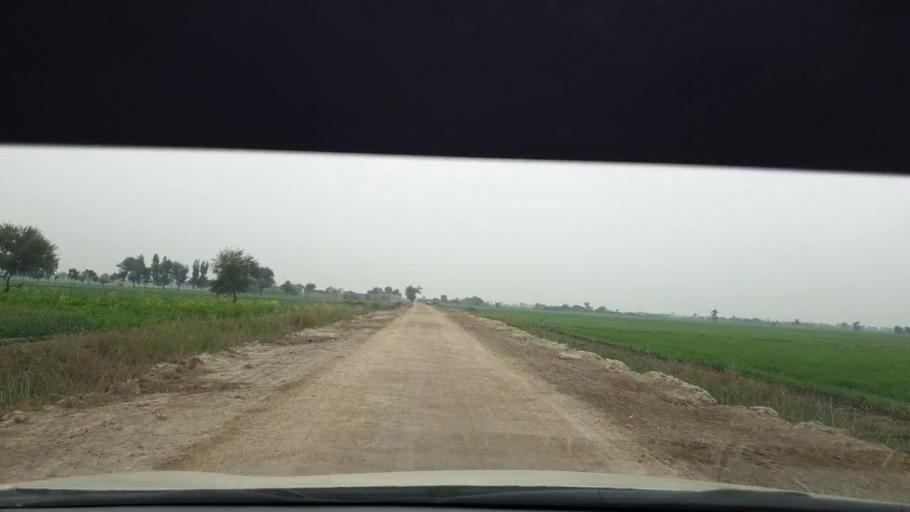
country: PK
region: Sindh
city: Berani
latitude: 25.7597
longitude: 68.8528
